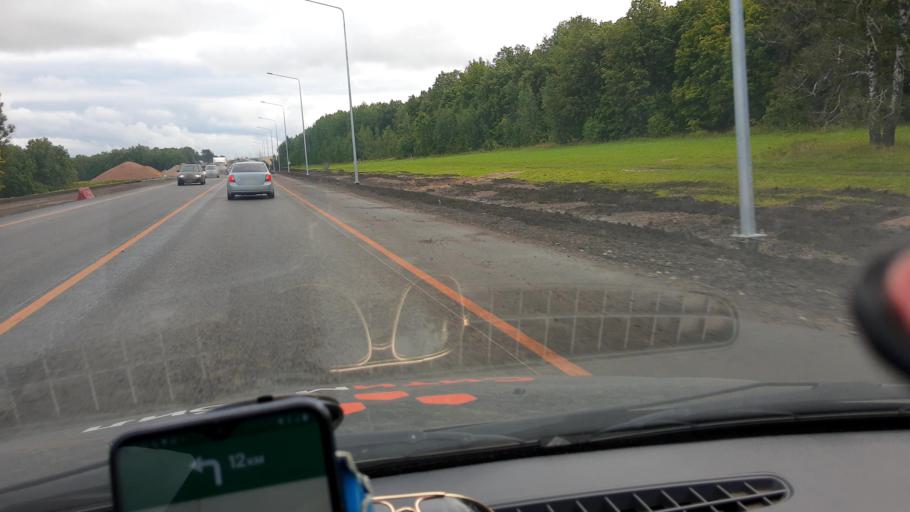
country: RU
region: Bashkortostan
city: Tolbazy
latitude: 54.1206
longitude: 55.9007
